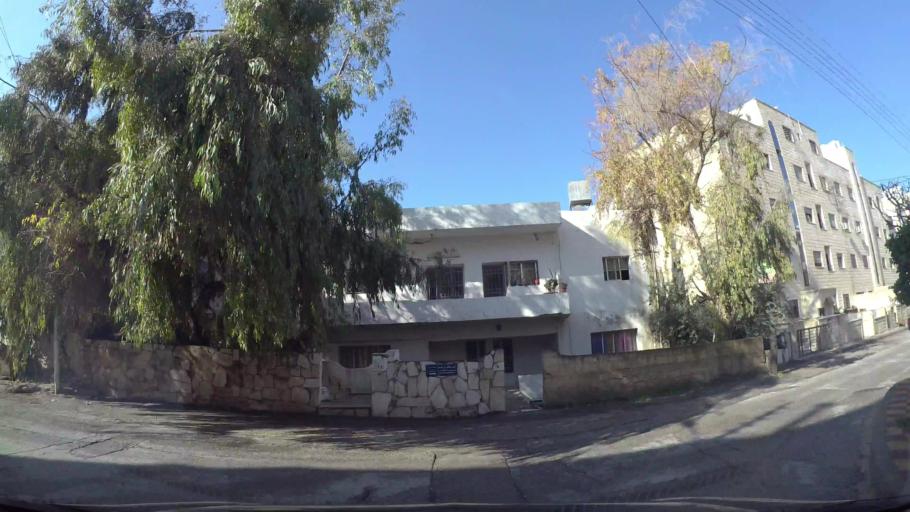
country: JO
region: Amman
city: Al Jubayhah
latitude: 31.9997
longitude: 35.8812
